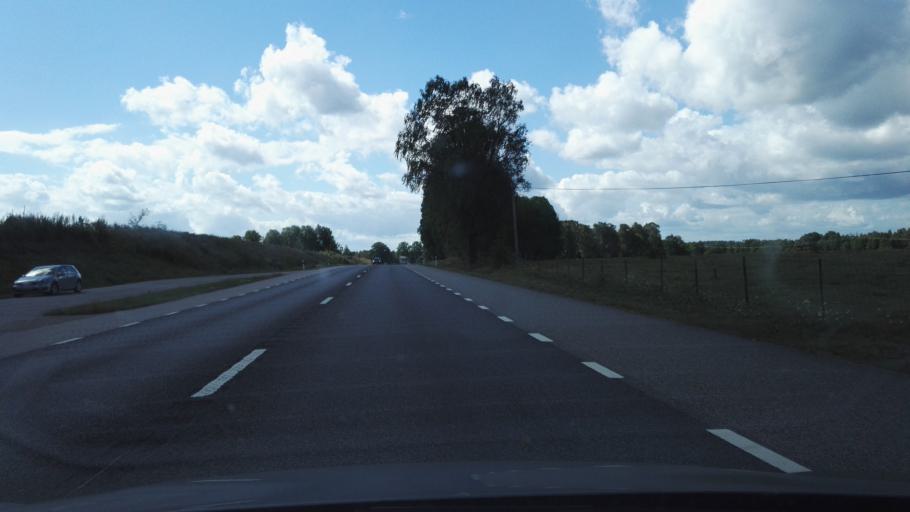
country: SE
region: Kronoberg
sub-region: Vaxjo Kommun
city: Vaexjoe
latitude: 56.8734
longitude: 14.7416
